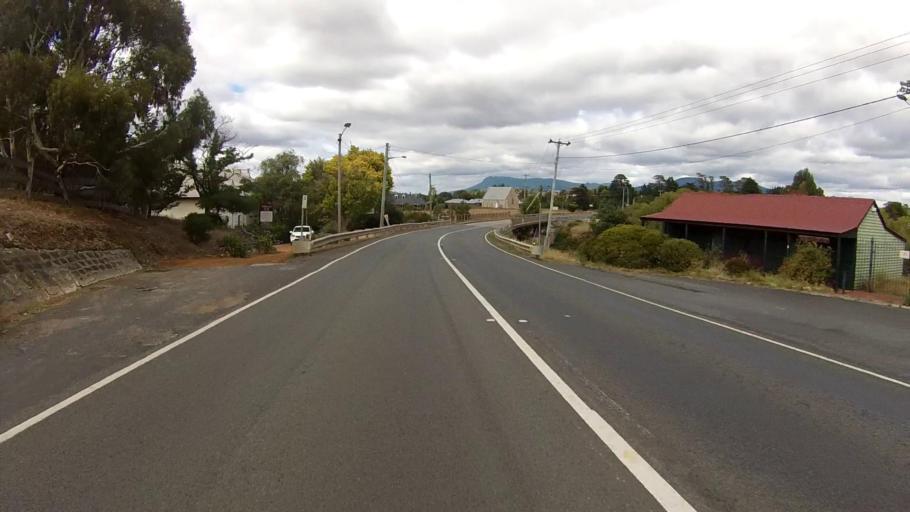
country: AU
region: Tasmania
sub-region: Brighton
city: Bridgewater
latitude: -42.6843
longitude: 147.2658
